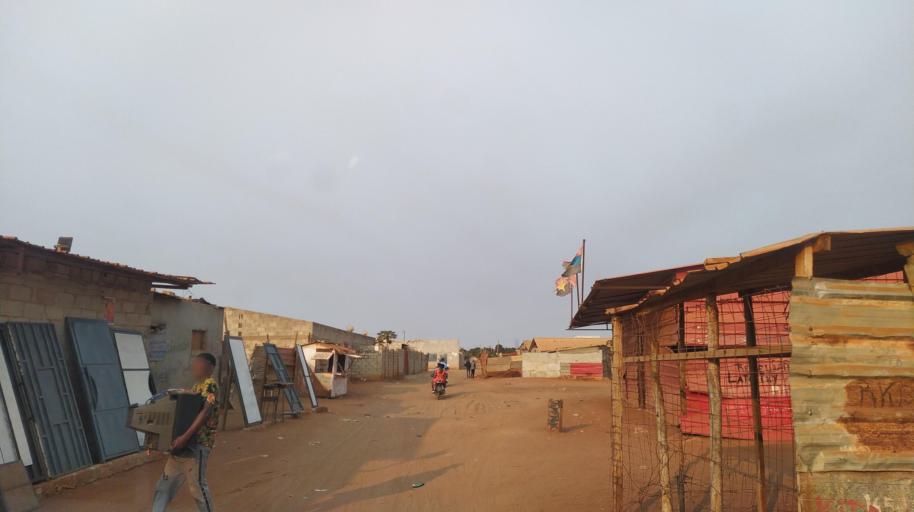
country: AO
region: Luanda
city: Luanda
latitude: -9.0733
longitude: 13.4195
